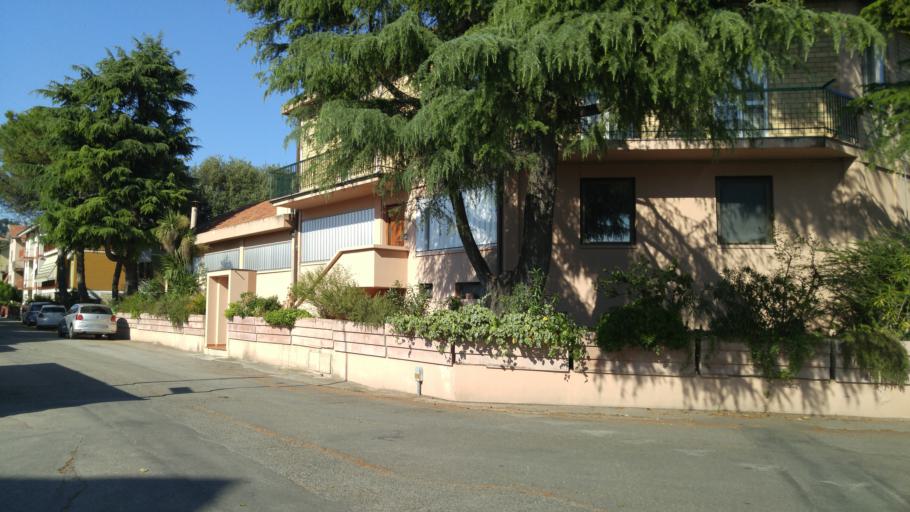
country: IT
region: The Marches
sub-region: Provincia di Pesaro e Urbino
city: Pesaro
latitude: 43.9082
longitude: 12.8863
